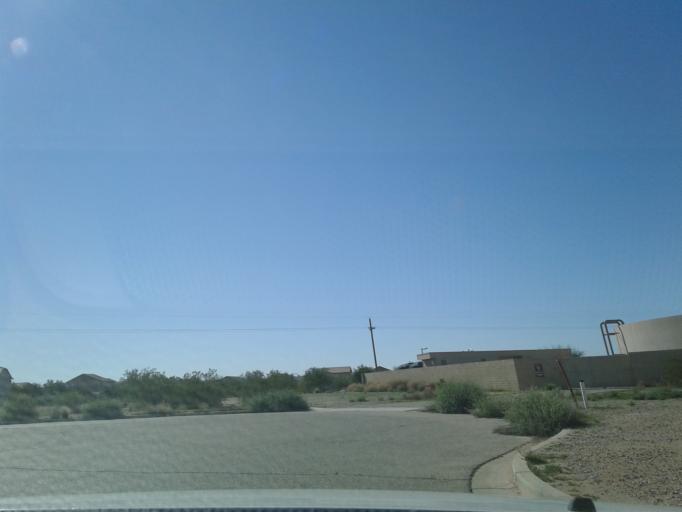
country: US
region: Arizona
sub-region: Pima County
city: Avra Valley
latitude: 32.5682
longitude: -111.3454
